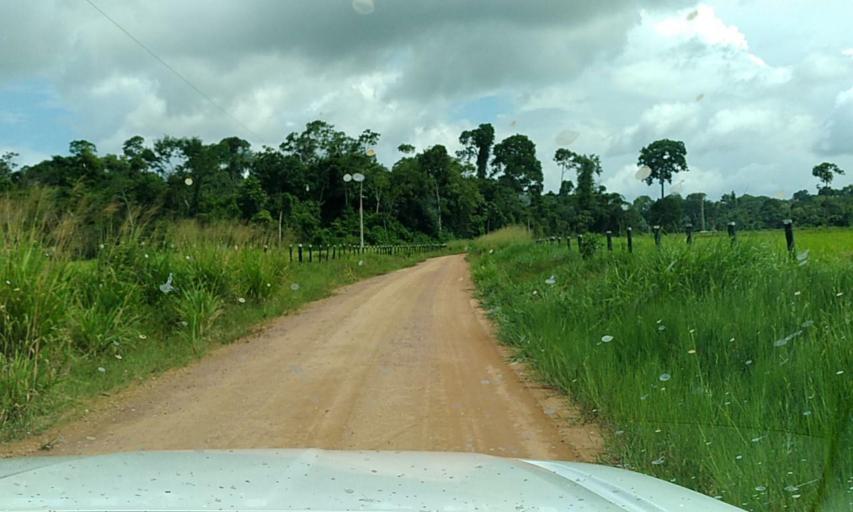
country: BR
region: Para
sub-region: Senador Jose Porfirio
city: Senador Jose Porfirio
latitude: -2.5156
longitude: -51.8396
